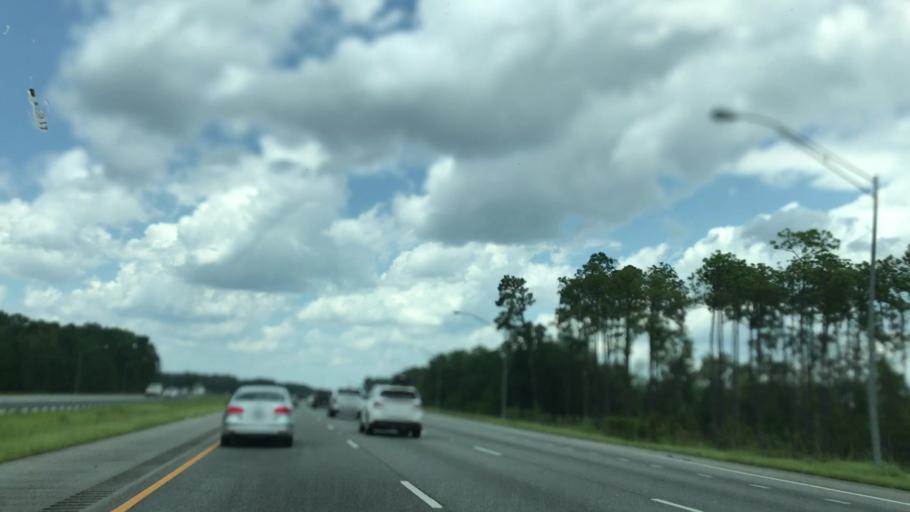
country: US
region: Georgia
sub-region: McIntosh County
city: Darien
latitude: 31.4713
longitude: -81.4461
